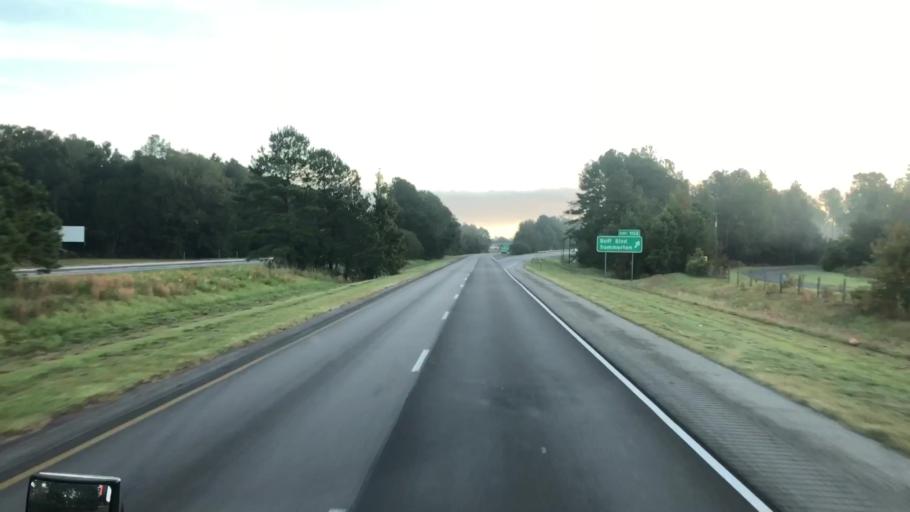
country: US
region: South Carolina
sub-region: Clarendon County
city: Manning
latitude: 33.5855
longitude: -80.3624
